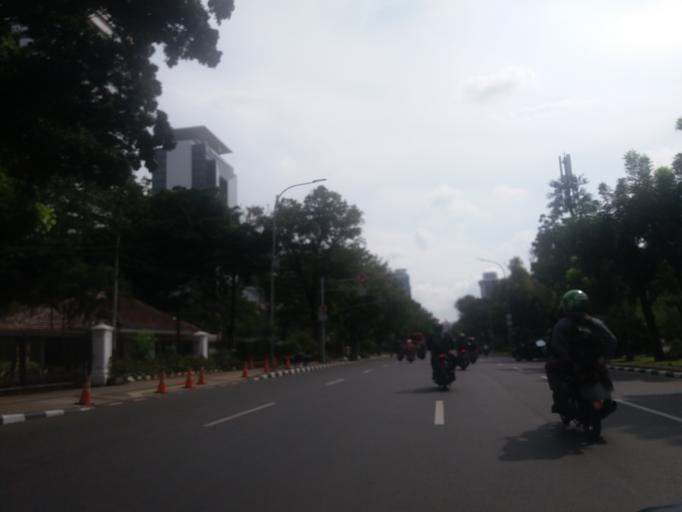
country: ID
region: Jakarta Raya
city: Jakarta
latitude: -6.1805
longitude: 106.8296
